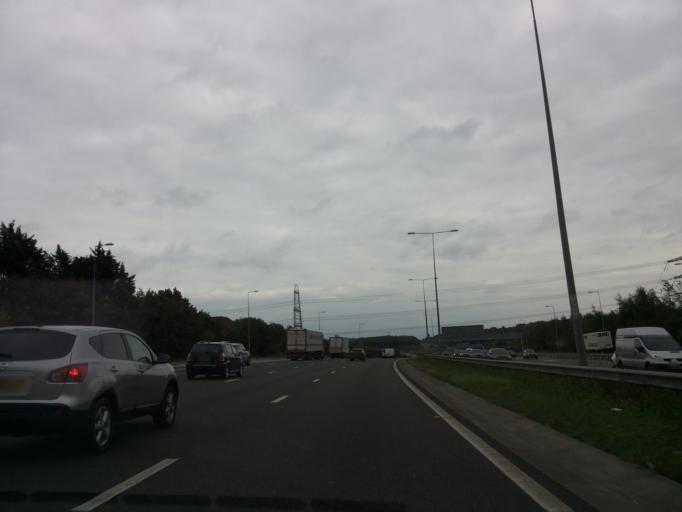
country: GB
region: England
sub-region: Kent
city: Gravesend
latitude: 51.4078
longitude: 0.3880
